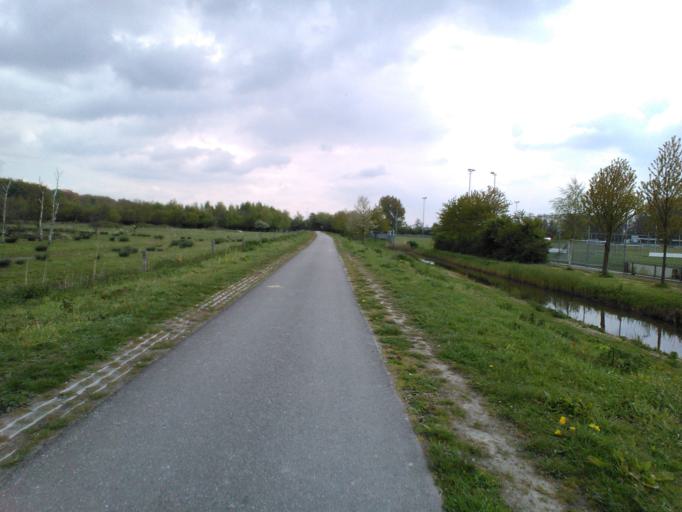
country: NL
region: South Holland
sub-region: Gemeente Vlaardingen
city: Vlaardingen
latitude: 51.9220
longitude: 4.3224
